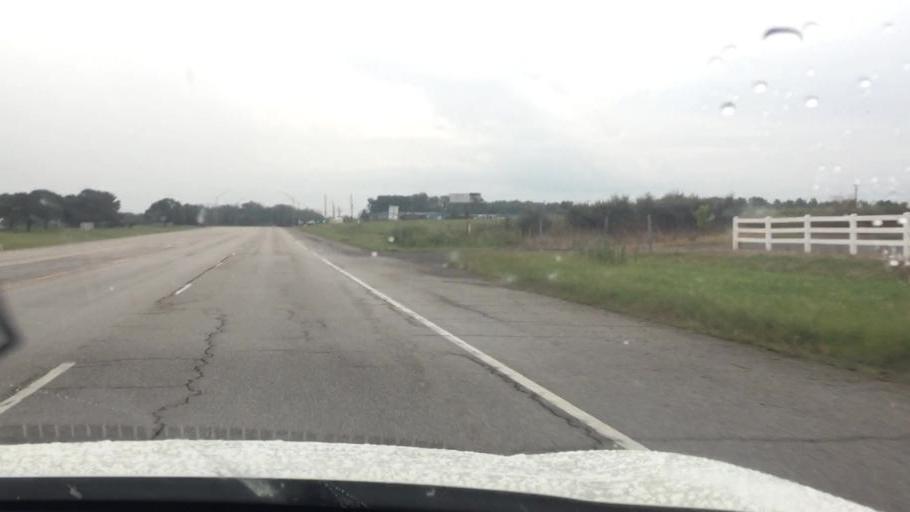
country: US
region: Ohio
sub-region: Champaign County
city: North Lewisburg
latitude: 40.2798
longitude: -83.5414
